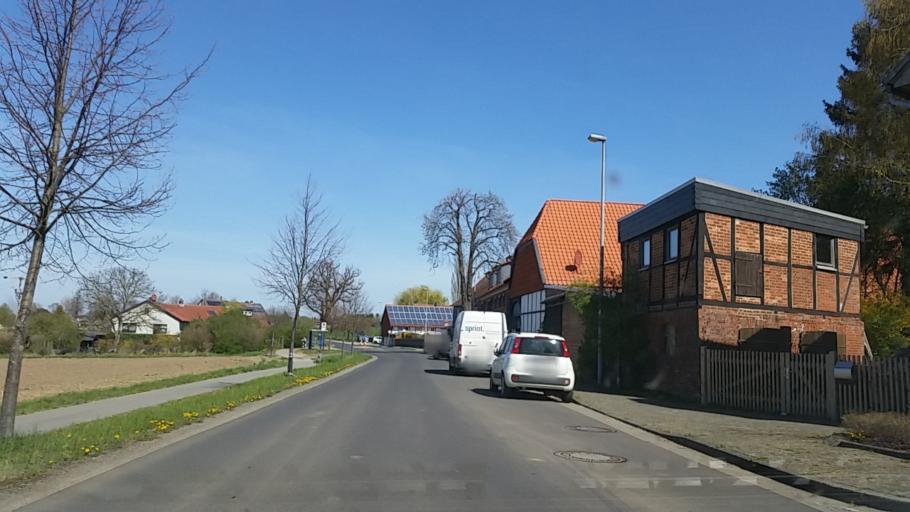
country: DE
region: Lower Saxony
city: Erkerode
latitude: 52.2275
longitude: 10.7019
